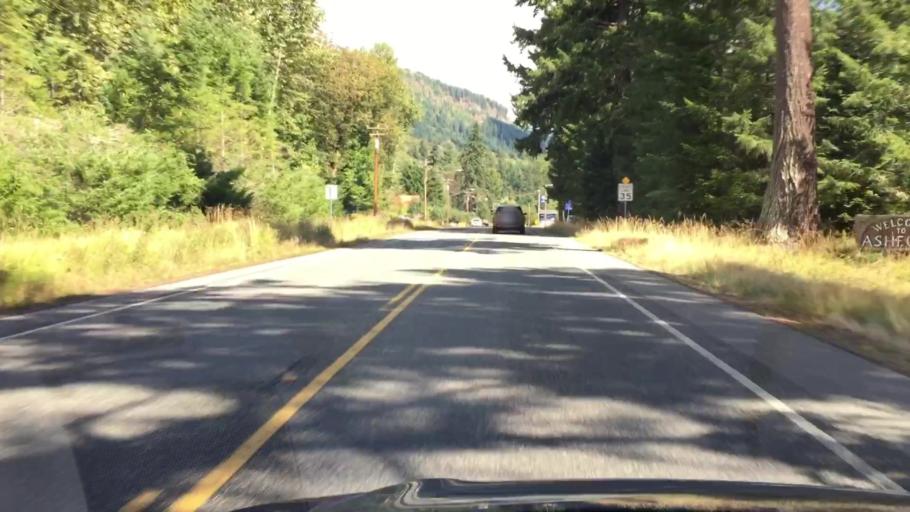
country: US
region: Washington
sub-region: Pierce County
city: Eatonville
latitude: 46.7595
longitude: -122.0426
